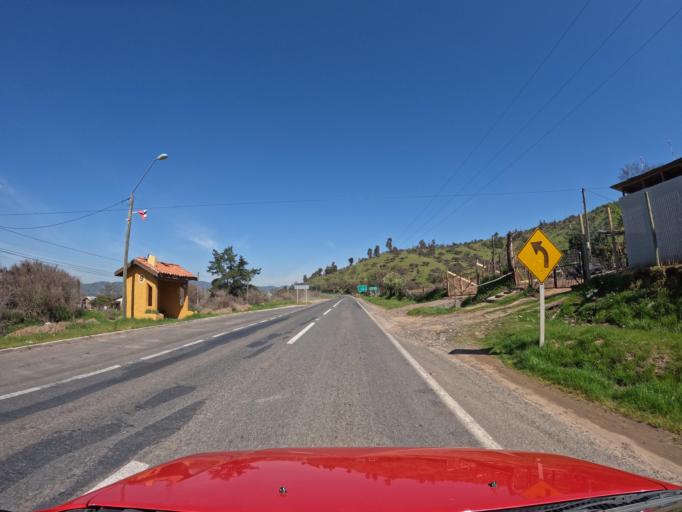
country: CL
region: Maule
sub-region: Provincia de Talca
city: Talca
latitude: -35.0844
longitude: -71.6423
